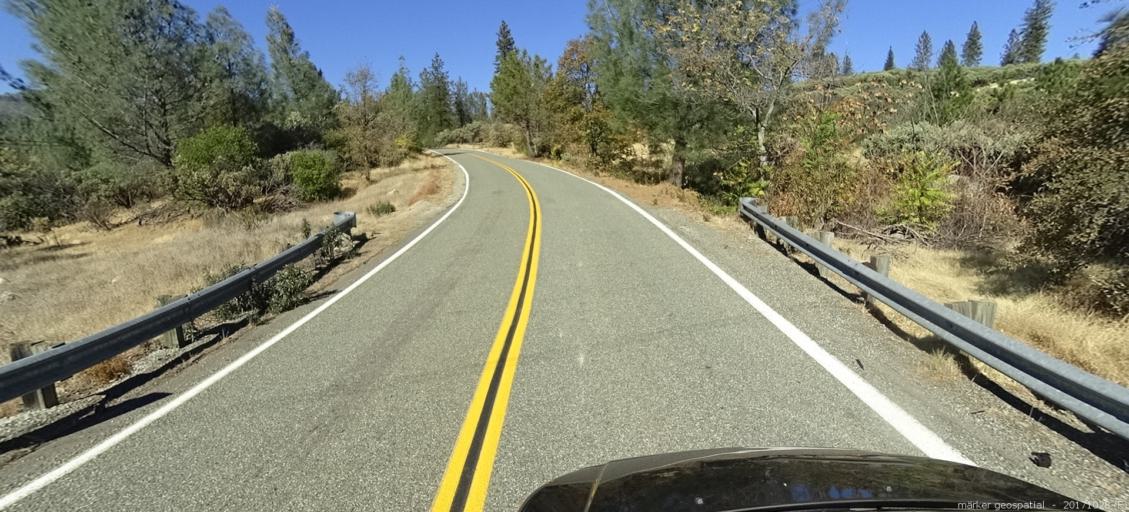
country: US
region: California
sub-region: Shasta County
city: Shasta
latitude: 40.6542
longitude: -122.4618
